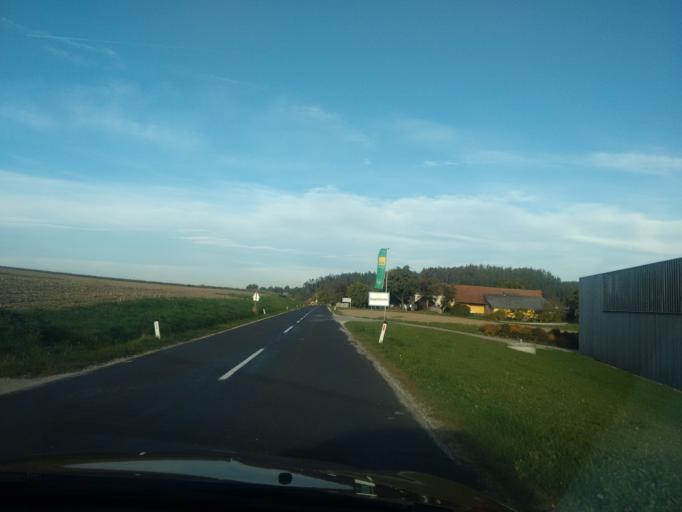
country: AT
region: Upper Austria
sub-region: Politischer Bezirk Vocklabruck
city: Niederthalheim
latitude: 48.1303
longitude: 13.7220
